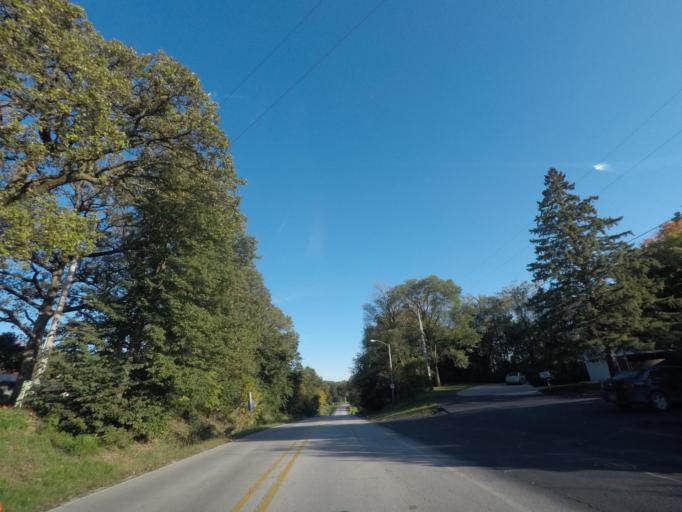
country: US
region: Iowa
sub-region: Story County
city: Nevada
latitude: 42.0162
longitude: -93.4629
